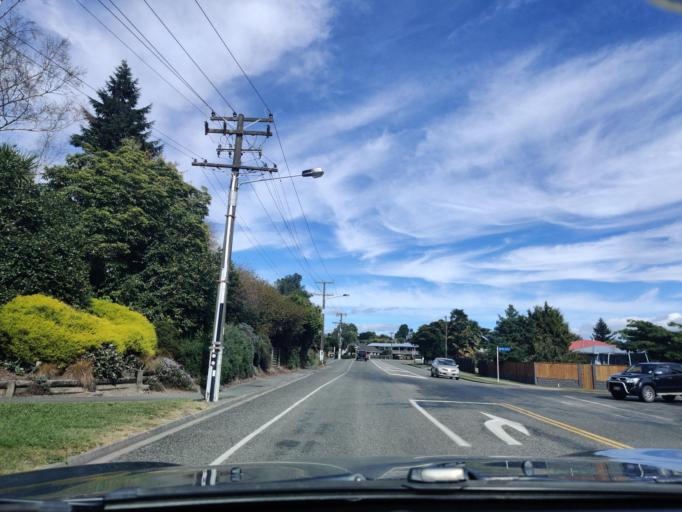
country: NZ
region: Tasman
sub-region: Tasman District
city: Wakefield
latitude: -41.4042
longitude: 173.0518
